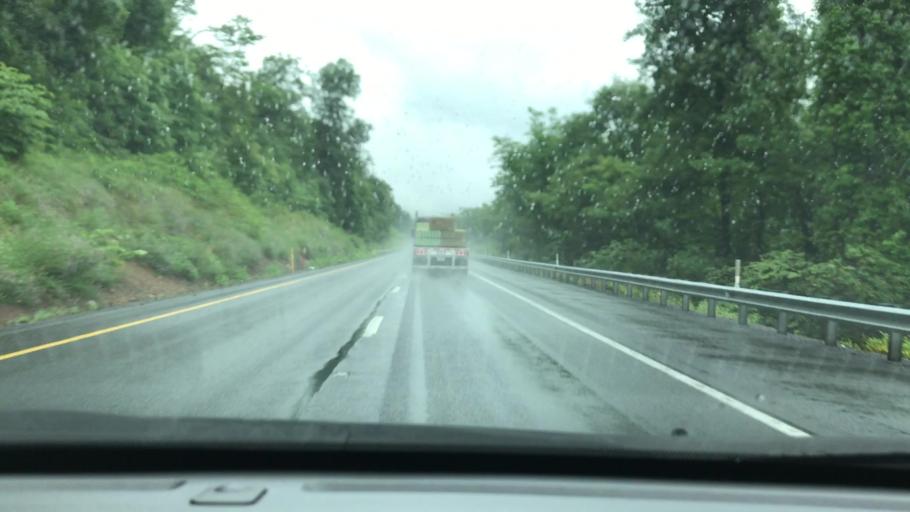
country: US
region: Maryland
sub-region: Washington County
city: Hancock
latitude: 39.8513
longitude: -78.2710
